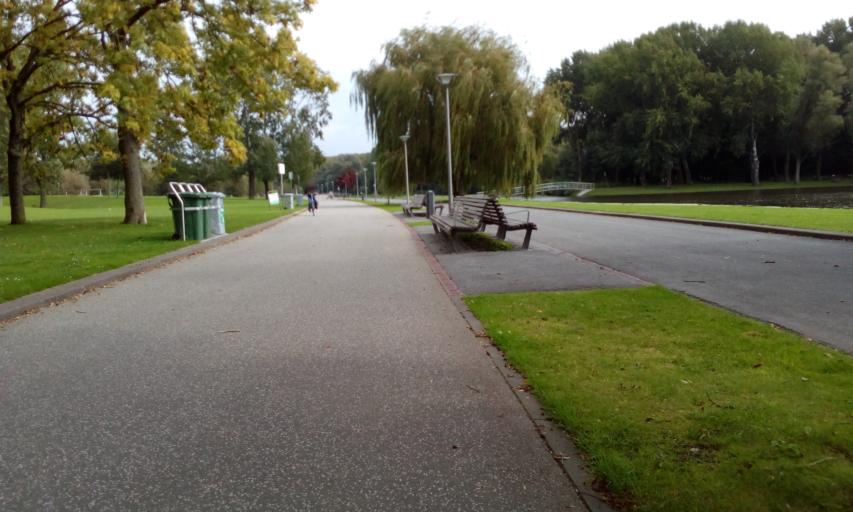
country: NL
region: South Holland
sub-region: Gemeente Rotterdam
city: Delfshaven
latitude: 51.8793
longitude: 4.4868
